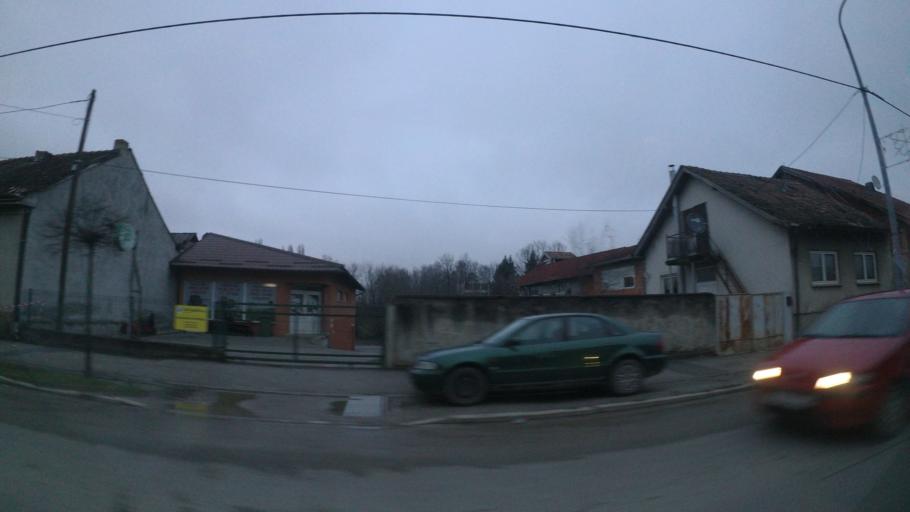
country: HR
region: Sisacko-Moslavacka
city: Petrinja
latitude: 45.4419
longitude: 16.2894
